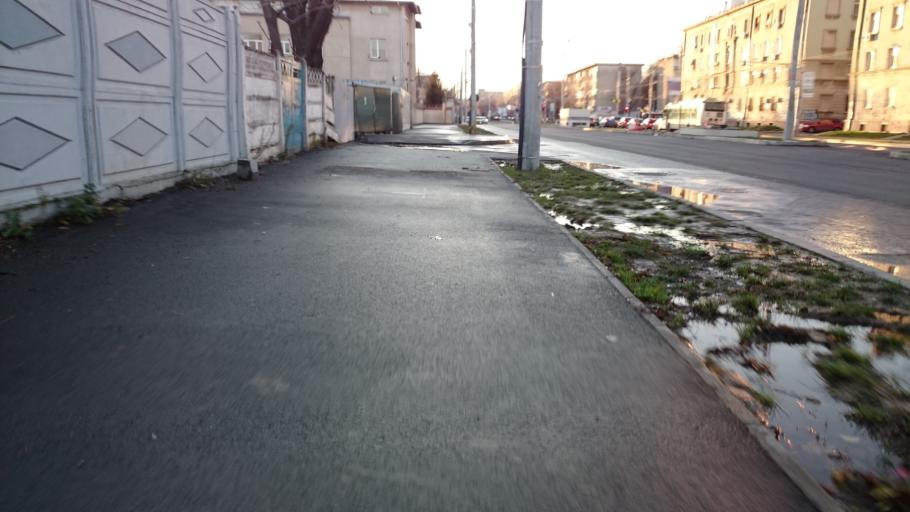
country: RO
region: Bucuresti
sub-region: Municipiul Bucuresti
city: Bucuresti
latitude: 44.4259
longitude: 26.0570
